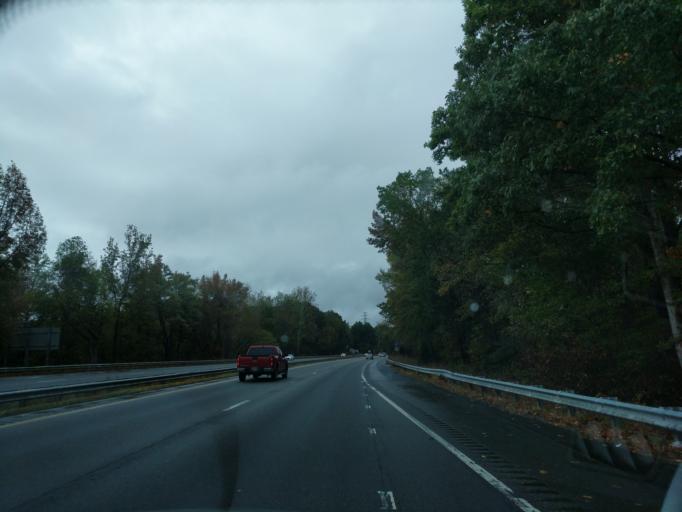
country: US
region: North Carolina
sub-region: Durham County
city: Gorman
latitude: 36.0278
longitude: -78.8489
